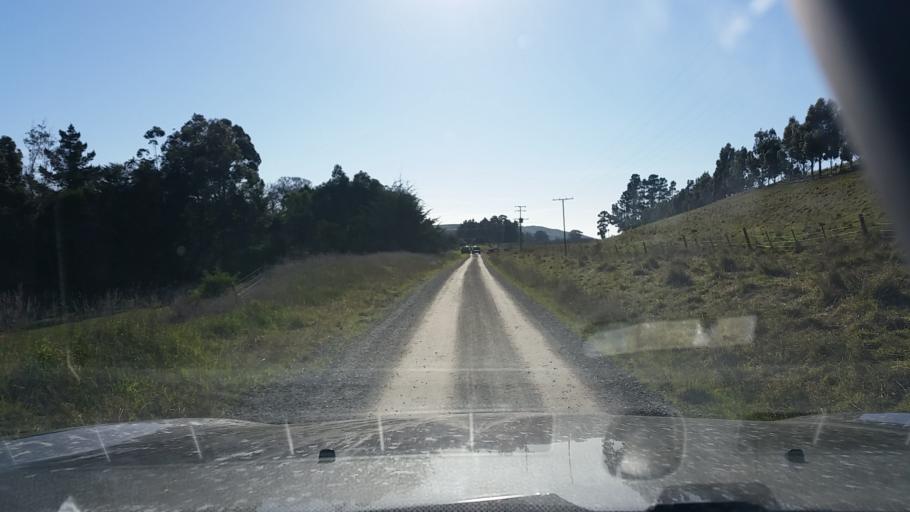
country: NZ
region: Marlborough
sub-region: Marlborough District
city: Blenheim
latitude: -41.6888
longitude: 174.1260
